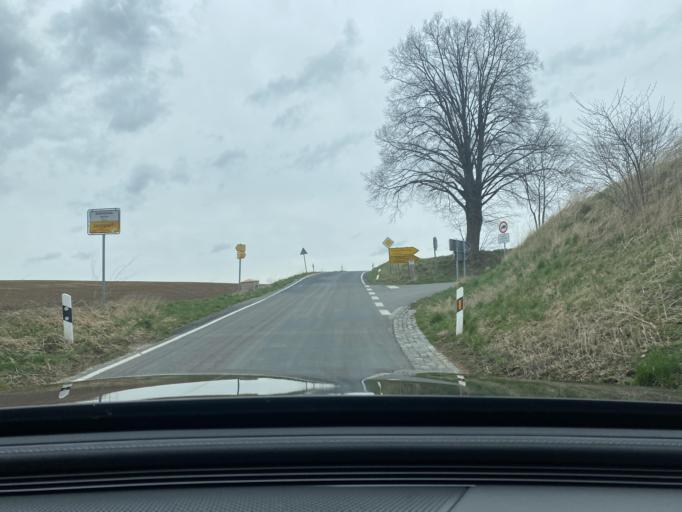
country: DE
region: Saxony
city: Goda
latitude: 51.1906
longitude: 14.3243
